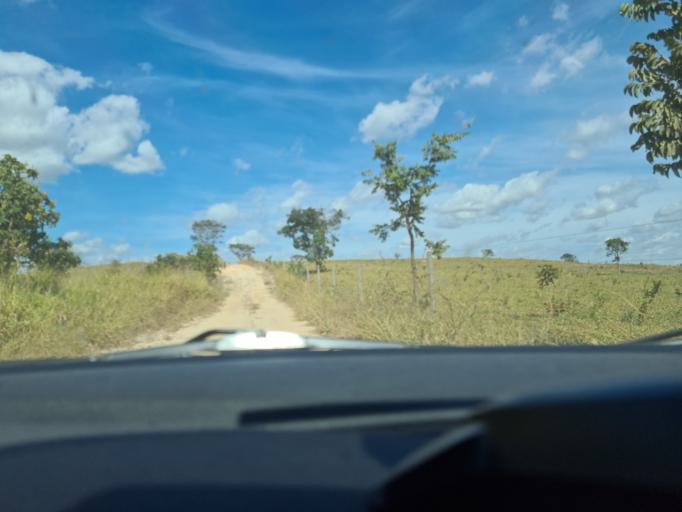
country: BR
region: Goias
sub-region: Silvania
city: Silvania
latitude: -16.5345
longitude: -48.5545
